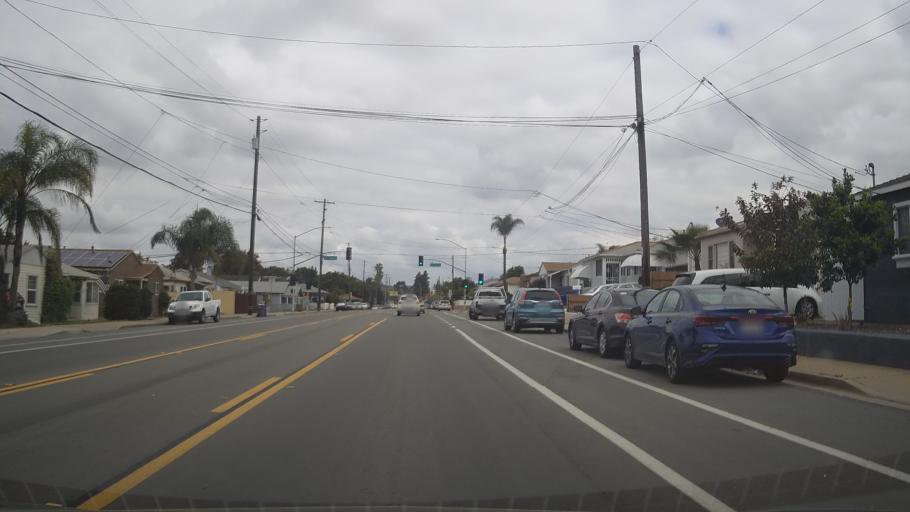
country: US
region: California
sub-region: San Diego County
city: La Mesa
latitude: 32.7624
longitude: -117.0468
